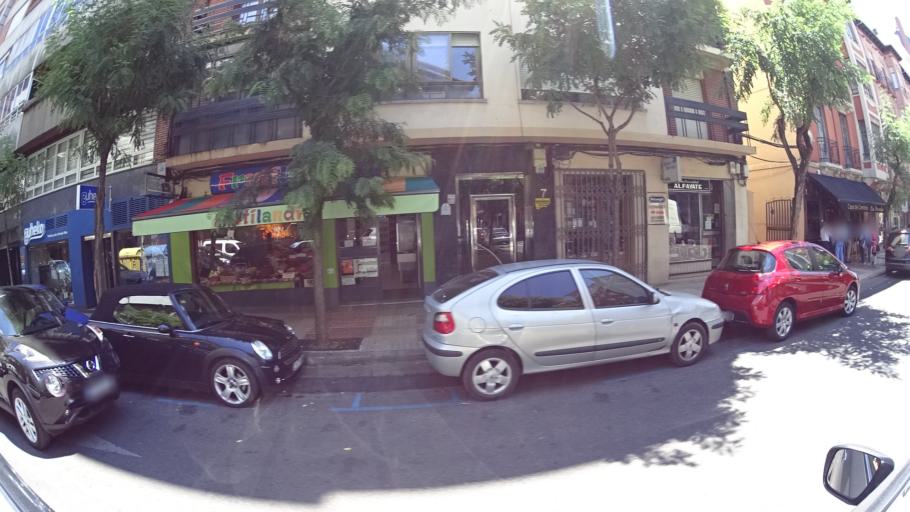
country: ES
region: Castille and Leon
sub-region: Provincia de Leon
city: Leon
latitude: 42.6007
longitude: -5.5750
